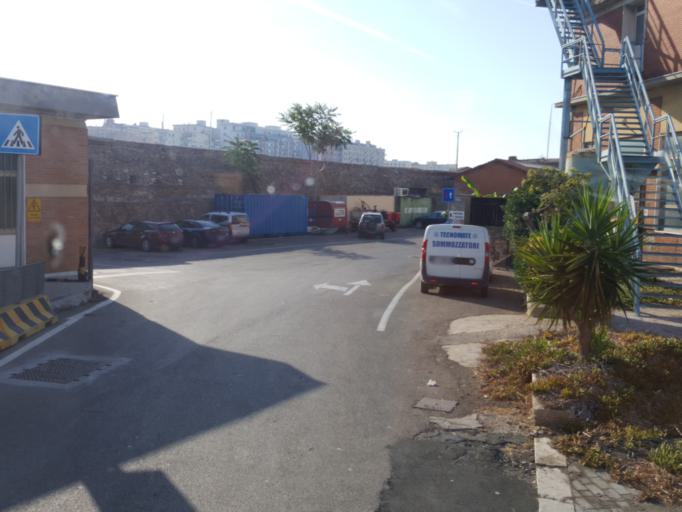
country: IT
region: Latium
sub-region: Citta metropolitana di Roma Capitale
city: Civitavecchia
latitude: 42.0952
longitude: 11.7865
